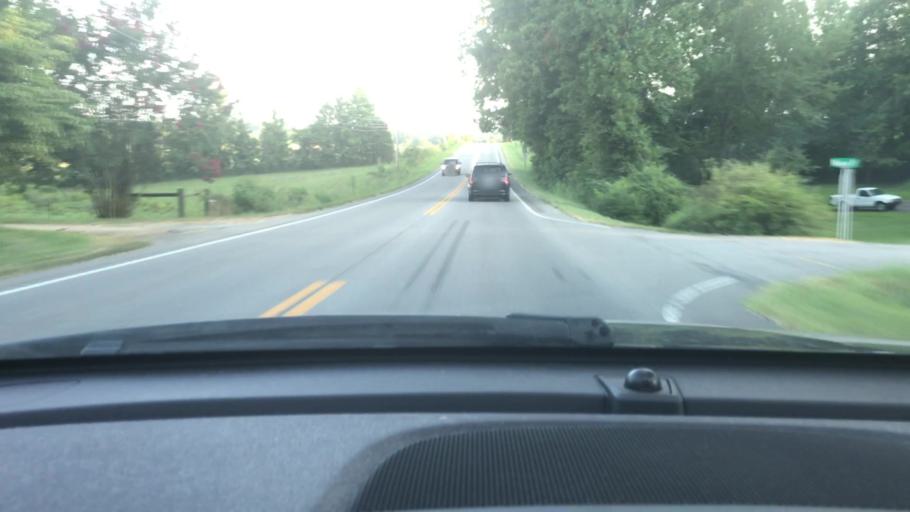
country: US
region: Tennessee
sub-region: Dickson County
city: Dickson
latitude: 36.0953
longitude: -87.3757
